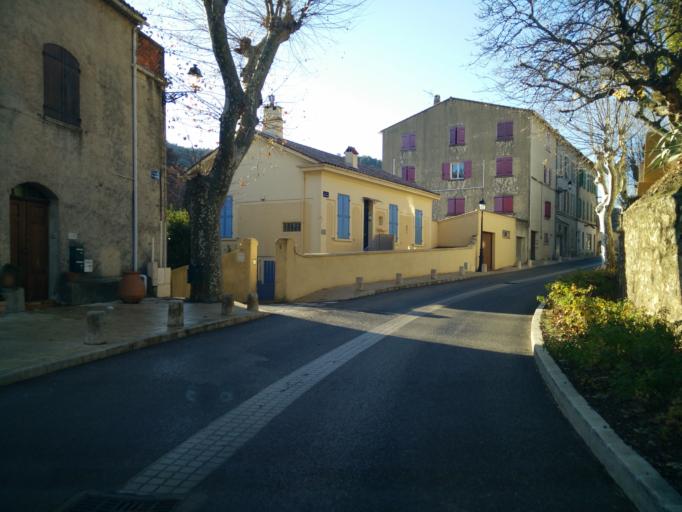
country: FR
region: Provence-Alpes-Cote d'Azur
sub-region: Departement du Var
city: Collobrieres
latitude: 43.2366
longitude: 6.3065
